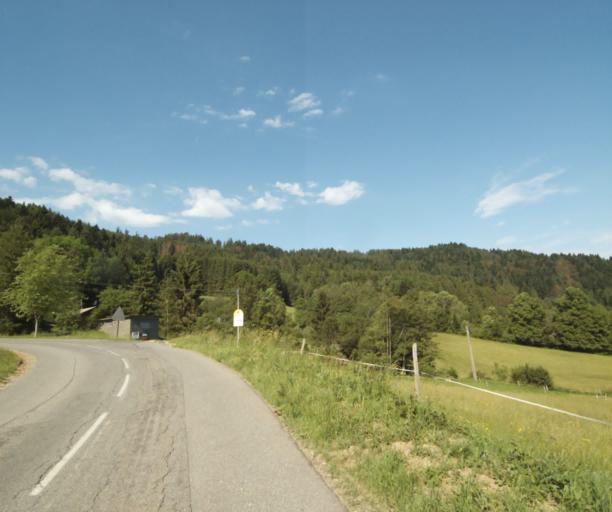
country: FR
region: Rhone-Alpes
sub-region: Departement de la Haute-Savoie
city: Lyaud
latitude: 46.3004
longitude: 6.5023
